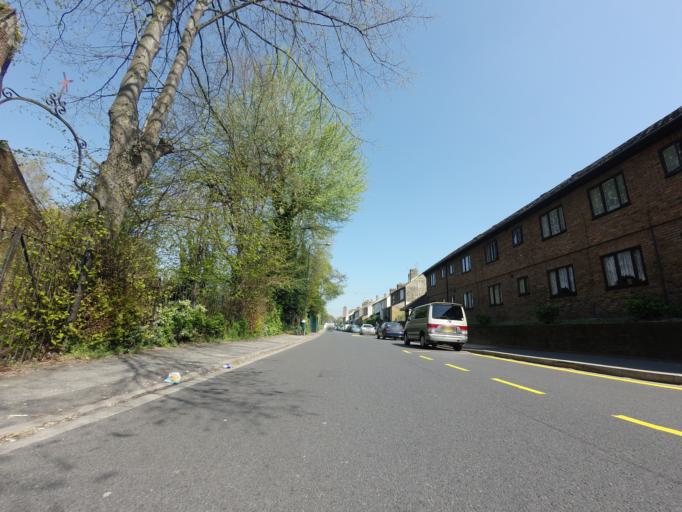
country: GB
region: England
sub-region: Greater London
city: Orpington
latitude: 51.3843
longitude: 0.1095
